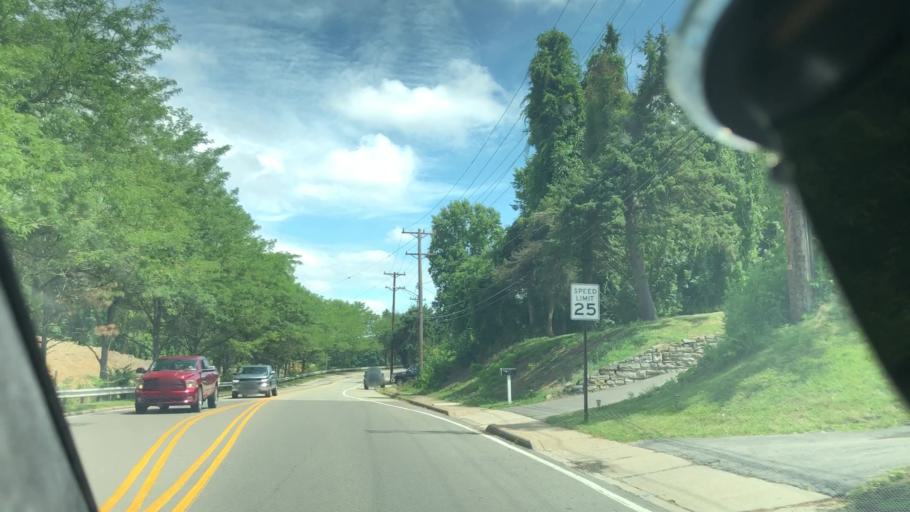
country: US
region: Pennsylvania
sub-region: Allegheny County
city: Mount Lebanon
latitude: 40.3625
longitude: -80.0637
